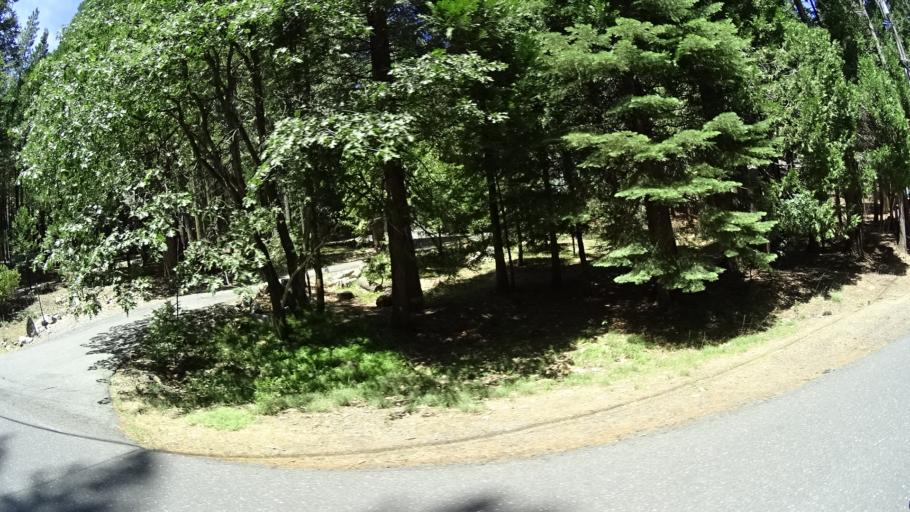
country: US
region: California
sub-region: Calaveras County
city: Arnold
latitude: 38.3083
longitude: -120.2593
